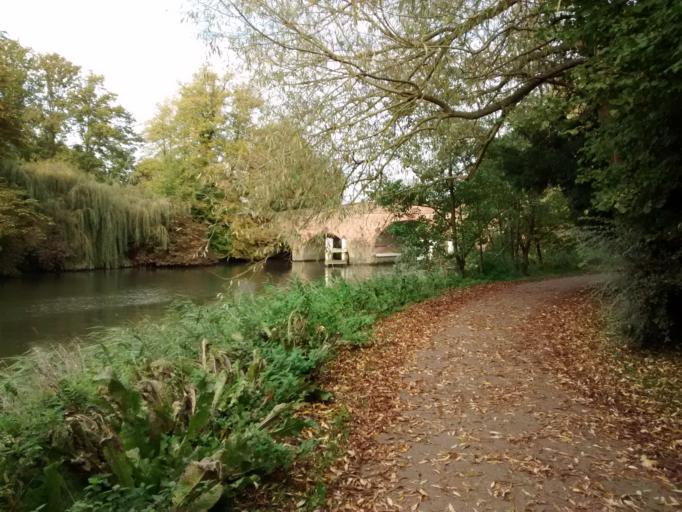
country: GB
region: England
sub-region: Wokingham
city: Sonning
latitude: 51.4751
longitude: -0.9141
